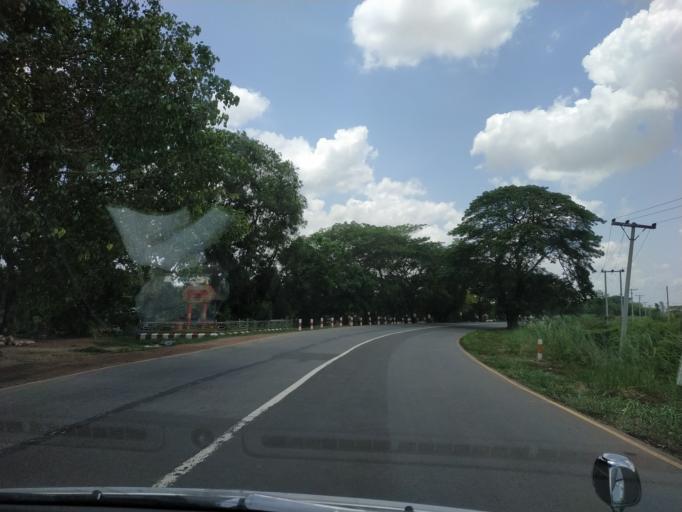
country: MM
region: Bago
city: Thanatpin
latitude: 17.4929
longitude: 96.6854
